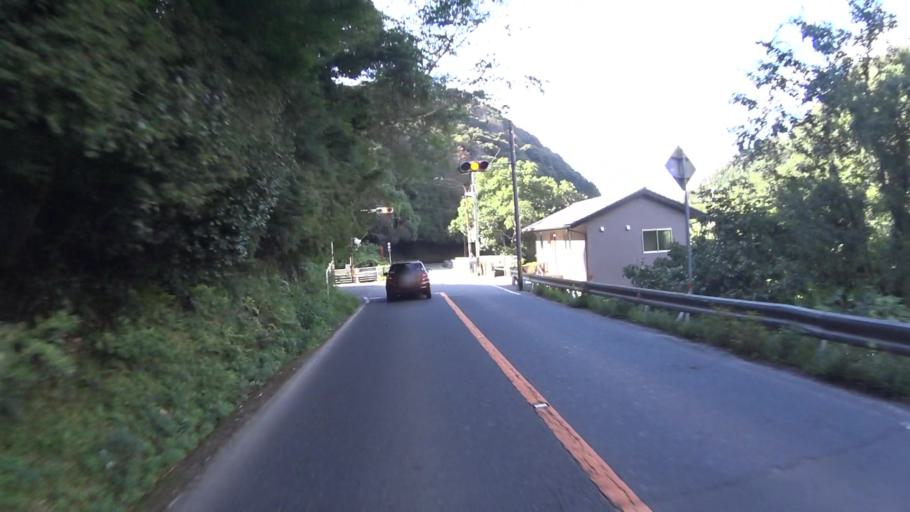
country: JP
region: Kyoto
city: Uji
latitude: 34.8825
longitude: 135.8163
